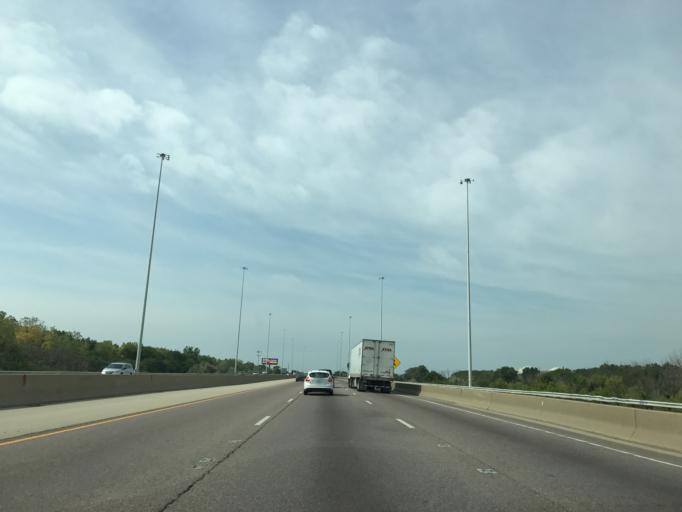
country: US
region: Illinois
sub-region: Cook County
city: Summit
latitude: 41.7905
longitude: -87.8240
